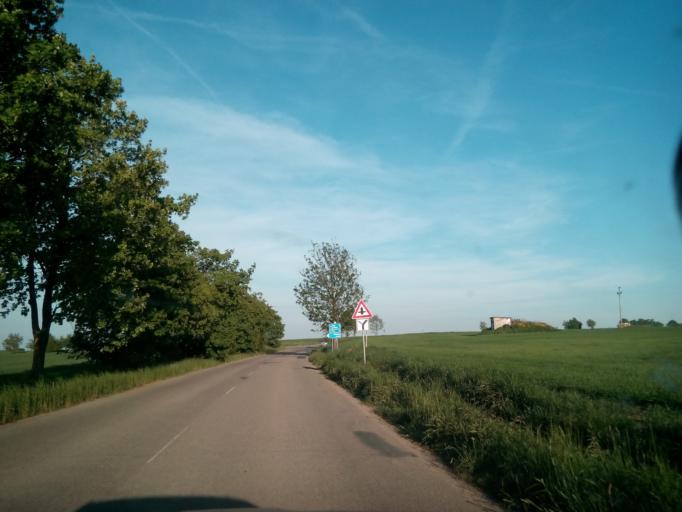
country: CZ
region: South Moravian
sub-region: Okres Blansko
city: Jedovnice
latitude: 49.3596
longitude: 16.7524
